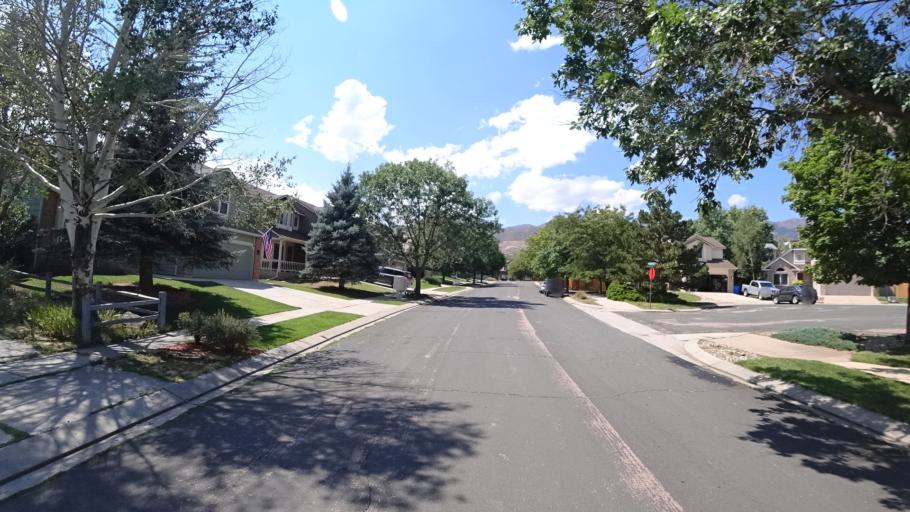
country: US
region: Colorado
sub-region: El Paso County
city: Air Force Academy
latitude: 38.9309
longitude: -104.8672
